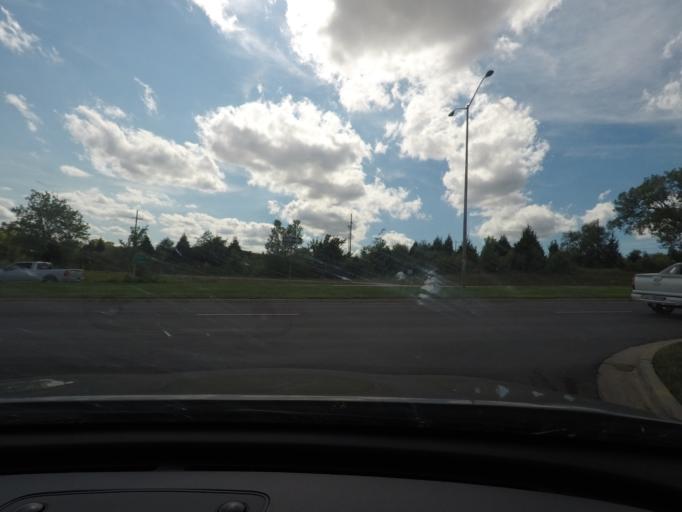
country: US
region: Kansas
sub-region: Johnson County
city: Olathe
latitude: 38.9437
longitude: -94.8159
